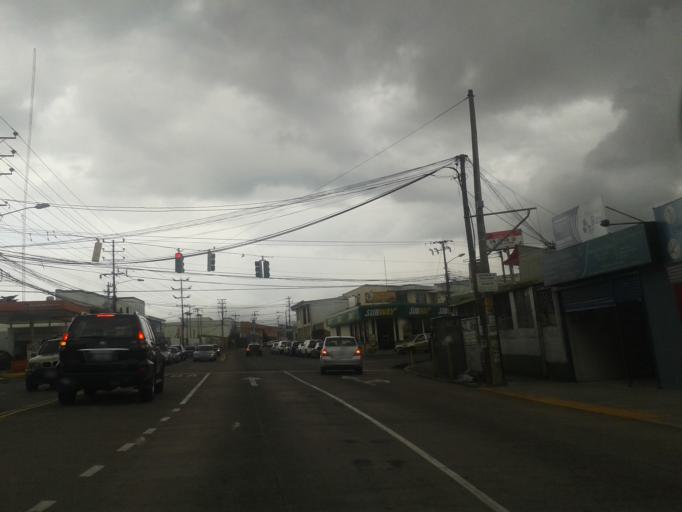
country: CR
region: San Jose
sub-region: Canton de Goicoechea
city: Guadalupe
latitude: 9.9499
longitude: -84.0593
